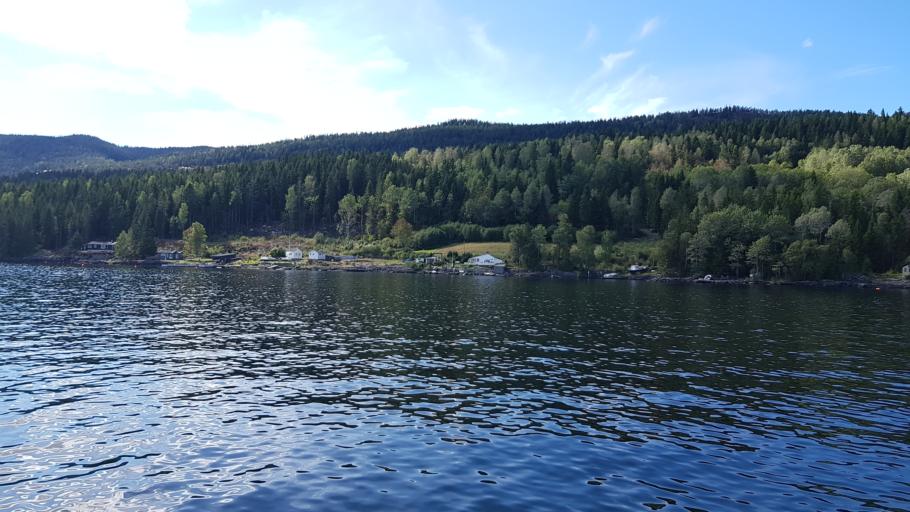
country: NO
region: Akershus
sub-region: Hurdal
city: Hurdal
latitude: 60.5448
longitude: 11.1985
